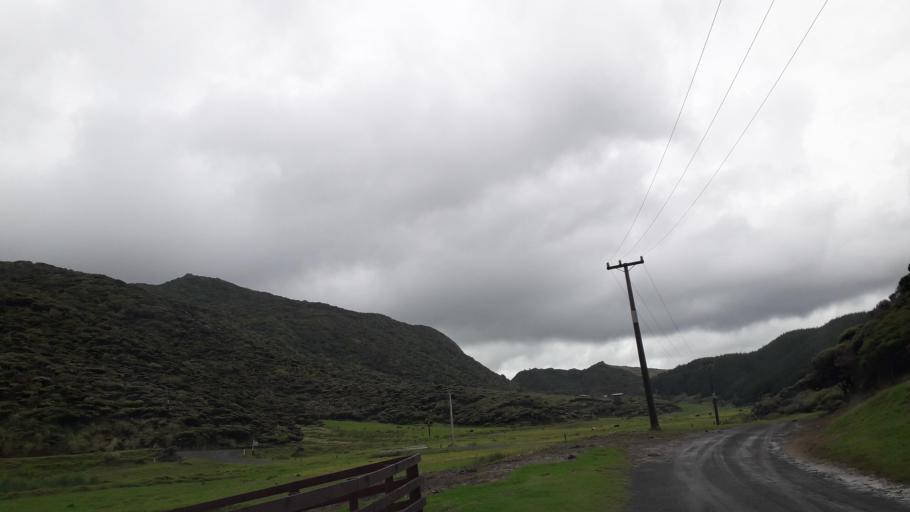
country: NZ
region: Northland
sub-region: Far North District
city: Ahipara
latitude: -35.4395
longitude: 173.2865
